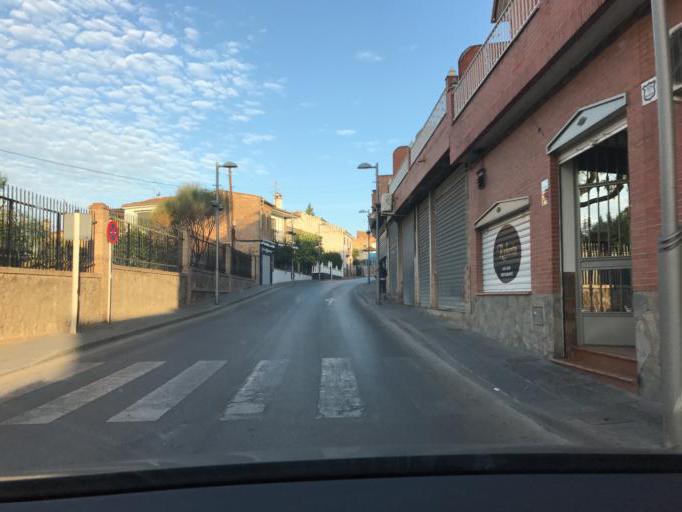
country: ES
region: Andalusia
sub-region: Provincia de Granada
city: Jun
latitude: 37.2195
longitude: -3.5931
